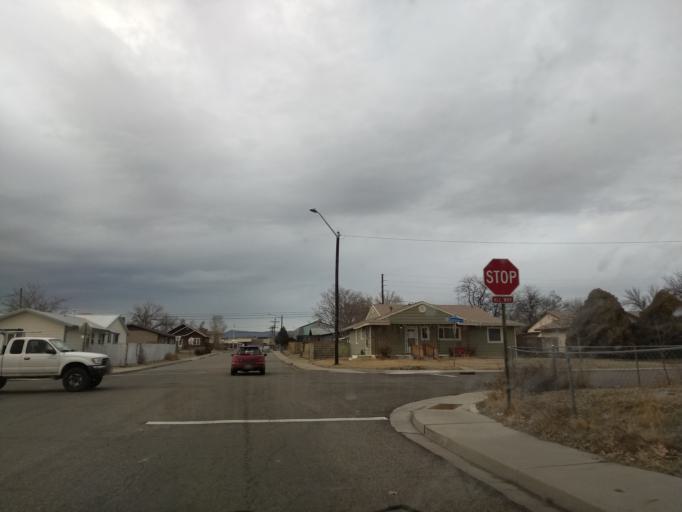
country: US
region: Colorado
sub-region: Mesa County
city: Grand Junction
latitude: 39.0731
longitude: -108.5374
